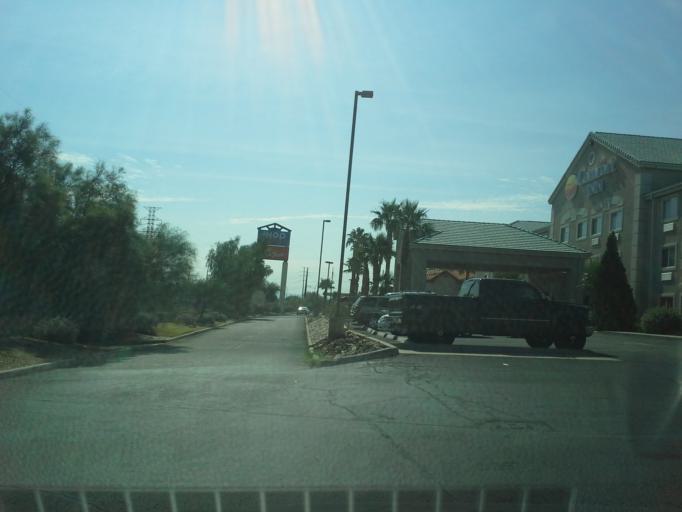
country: US
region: Arizona
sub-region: Pima County
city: Flowing Wells
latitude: 32.2526
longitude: -110.9989
